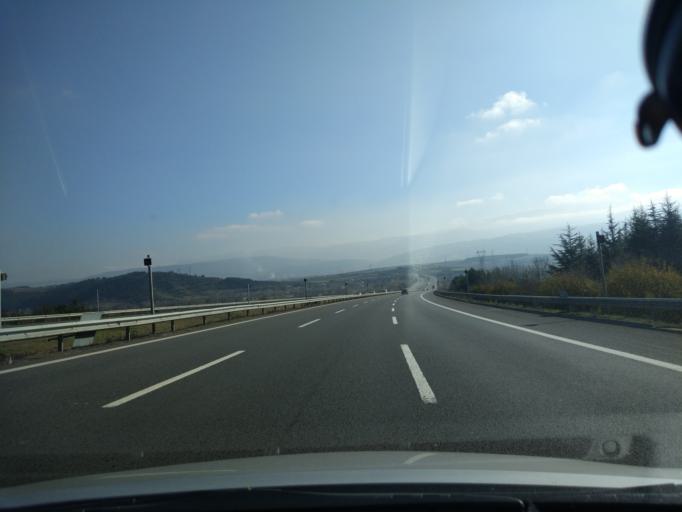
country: TR
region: Bolu
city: Bolu
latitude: 40.7784
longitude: 31.7222
